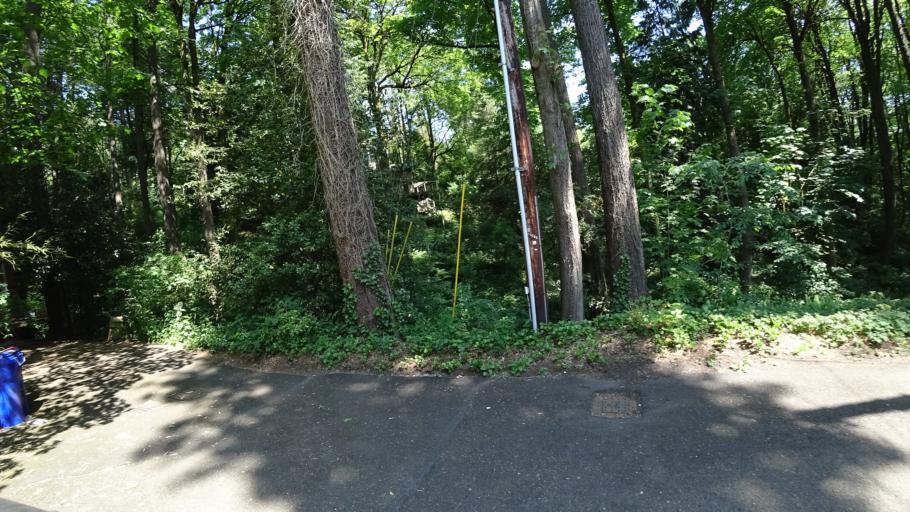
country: US
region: Oregon
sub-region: Washington County
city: West Haven-Sylvan
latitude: 45.5207
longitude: -122.7255
